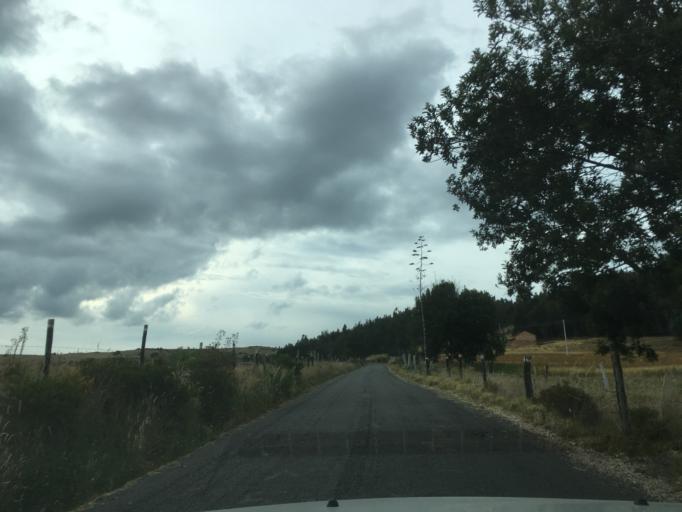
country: CO
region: Boyaca
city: Firavitoba
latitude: 5.6792
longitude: -73.0225
